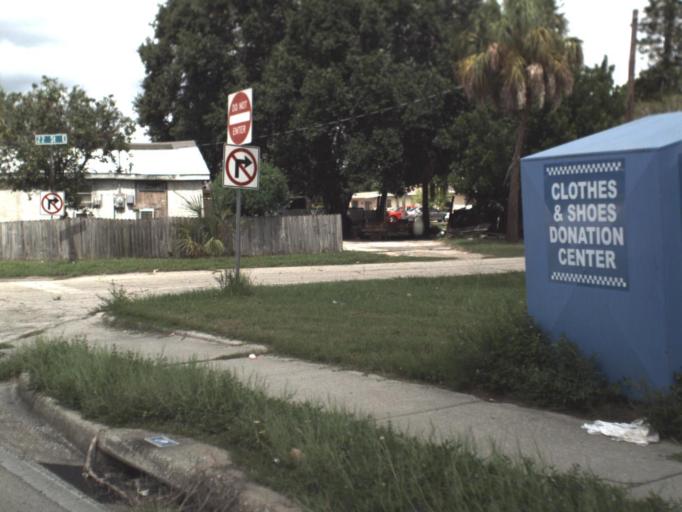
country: US
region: Florida
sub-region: Manatee County
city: Memphis
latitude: 27.5329
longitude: -82.5609
